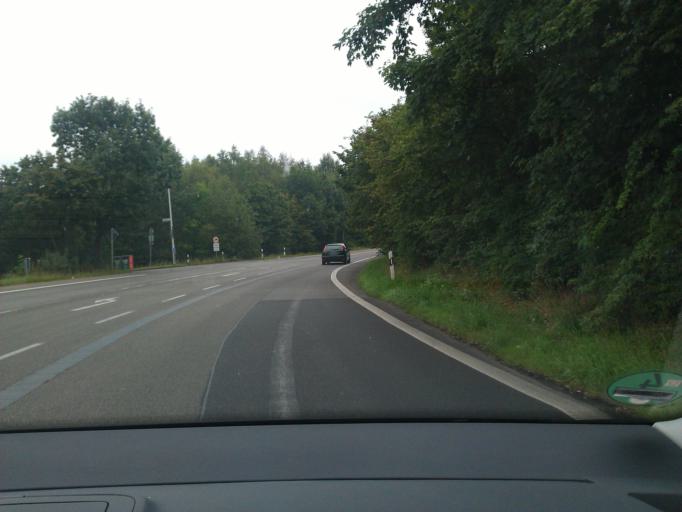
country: DE
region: North Rhine-Westphalia
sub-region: Regierungsbezirk Dusseldorf
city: Hilden
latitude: 51.1893
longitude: 6.9226
